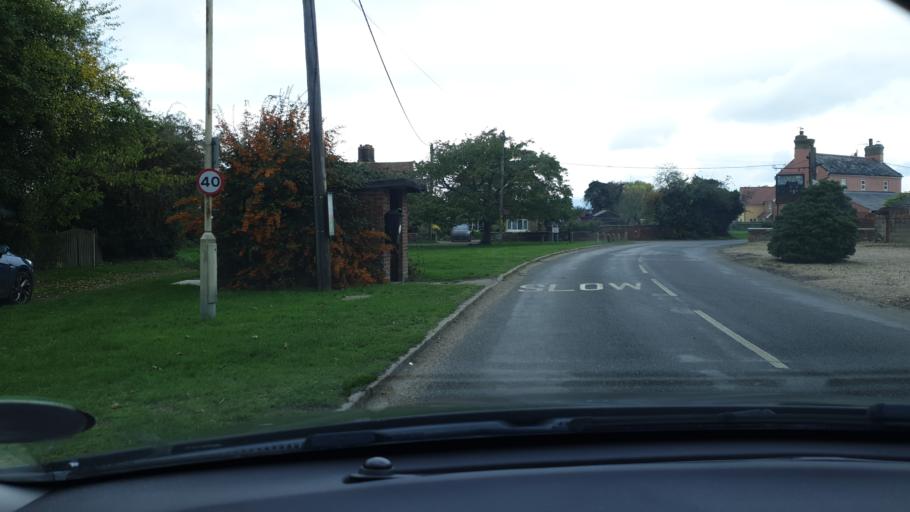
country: GB
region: England
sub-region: Essex
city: Mistley
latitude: 51.9339
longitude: 1.0940
